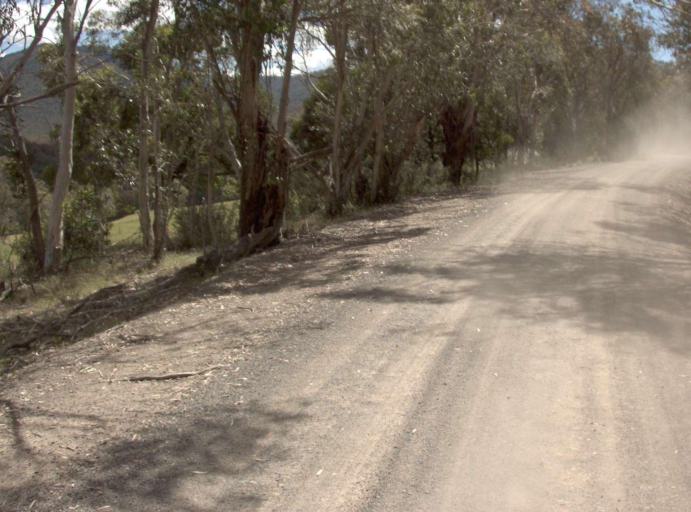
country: AU
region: New South Wales
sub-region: Bombala
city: Bombala
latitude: -37.1484
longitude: 148.6633
